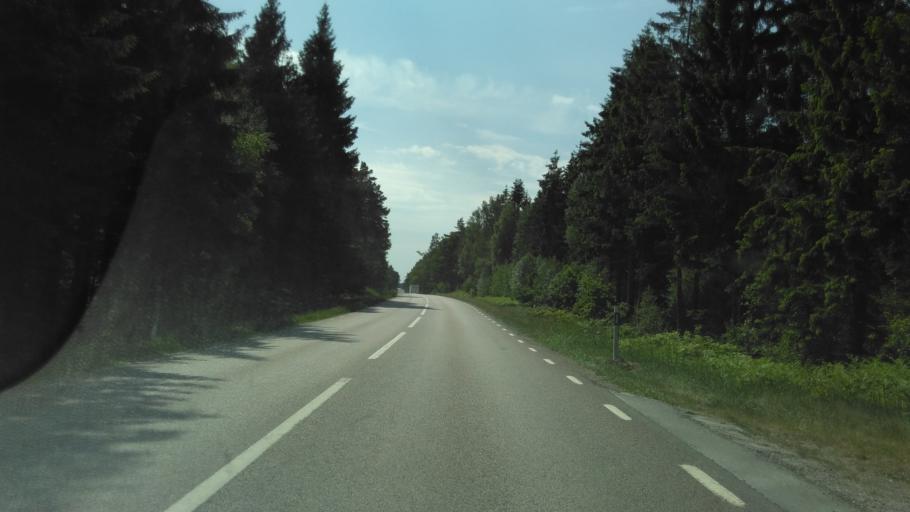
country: SE
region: Vaestra Goetaland
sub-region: Vara Kommun
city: Vara
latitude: 58.4323
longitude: 12.8967
